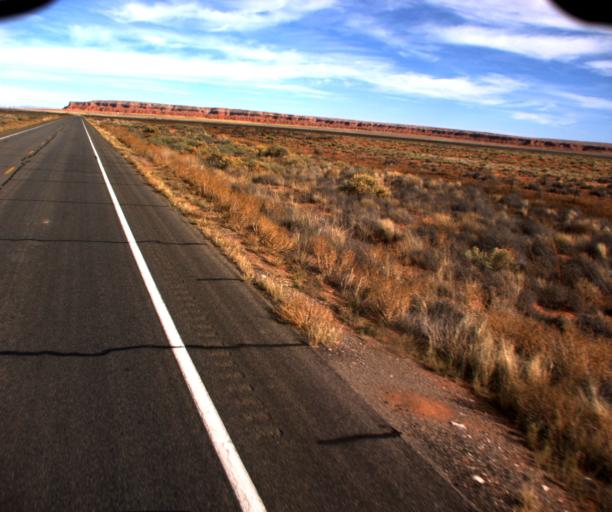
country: US
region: Arizona
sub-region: Navajo County
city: Kayenta
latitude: 36.7798
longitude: -109.9955
